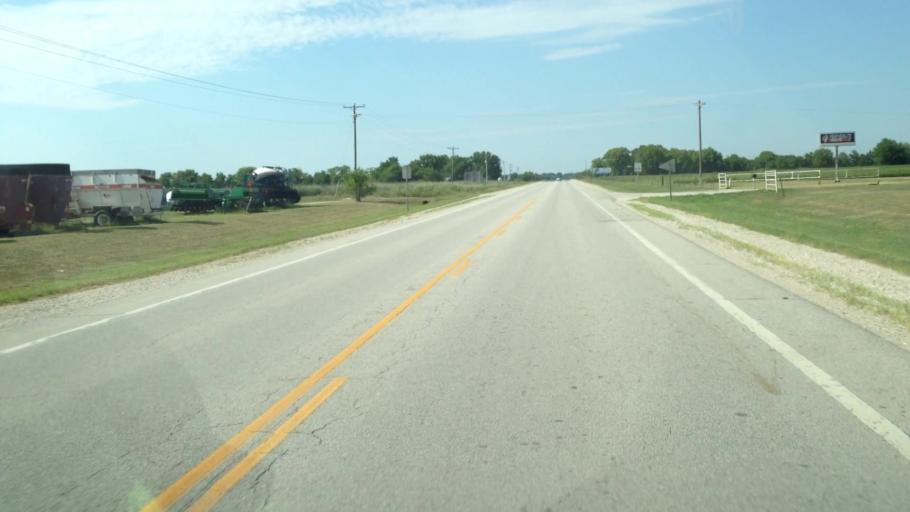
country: US
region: Kansas
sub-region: Neosho County
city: Erie
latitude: 37.5183
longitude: -95.2700
